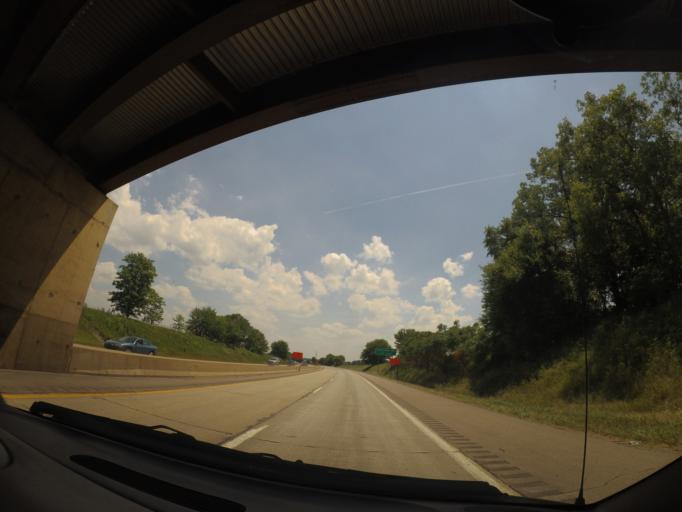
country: US
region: Indiana
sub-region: Saint Joseph County
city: South Bend
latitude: 41.6646
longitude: -86.3393
